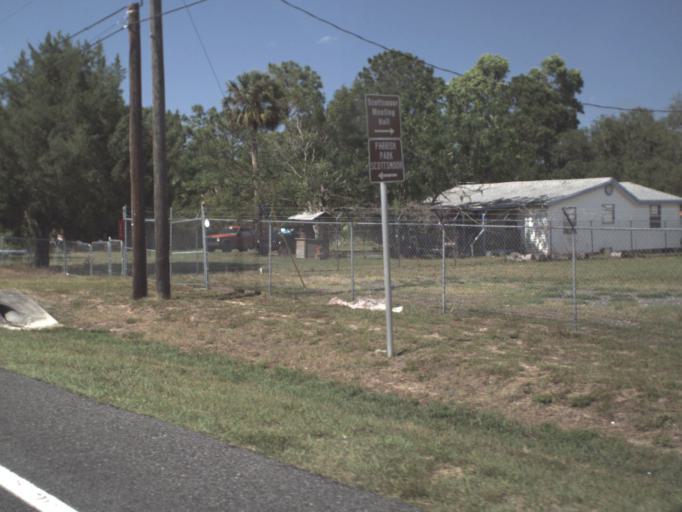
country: US
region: Florida
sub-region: Volusia County
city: Oak Hill
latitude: 28.7646
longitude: -80.8769
